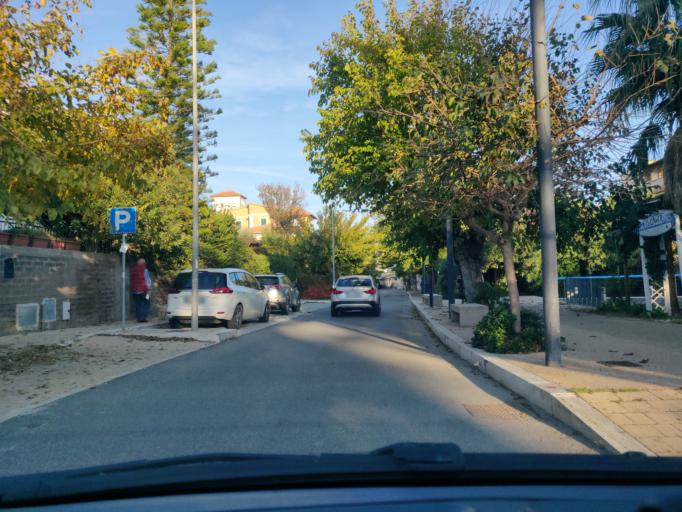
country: IT
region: Latium
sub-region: Citta metropolitana di Roma Capitale
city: Santa Marinella
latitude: 42.0327
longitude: 11.8528
